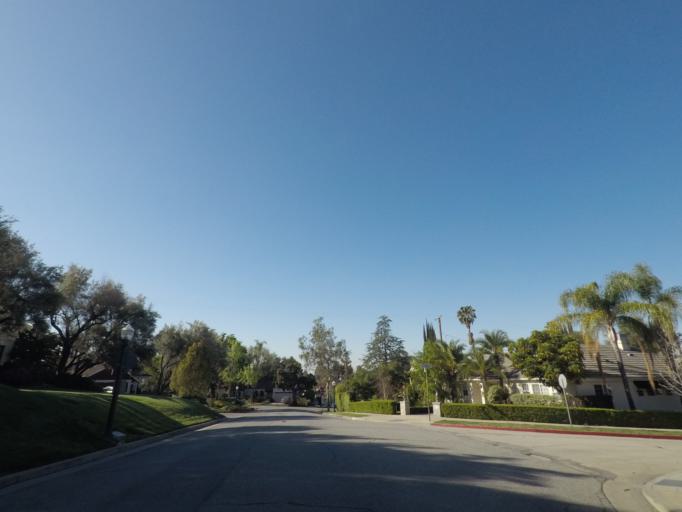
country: US
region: California
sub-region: Los Angeles County
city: North Glendale
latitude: 34.1617
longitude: -118.2419
